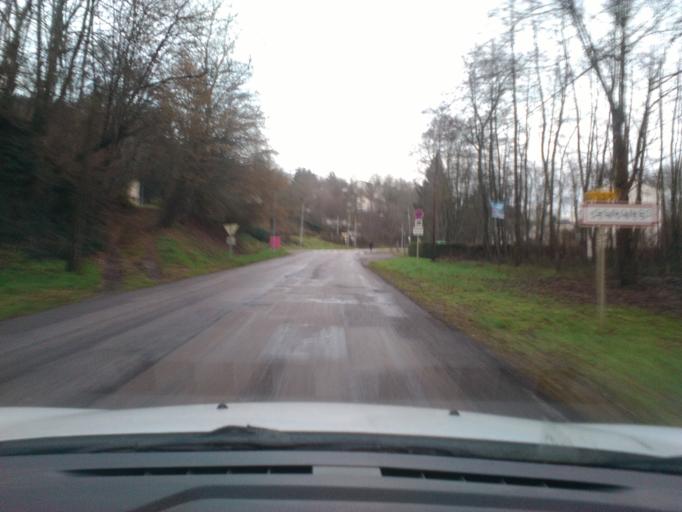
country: FR
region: Lorraine
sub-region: Departement des Vosges
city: Senones
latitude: 48.3920
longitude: 6.9633
